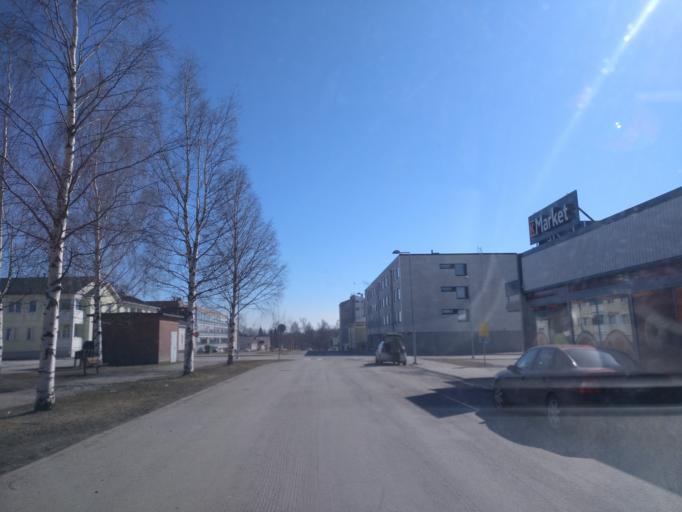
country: FI
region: Lapland
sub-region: Kemi-Tornio
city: Kemi
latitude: 65.7342
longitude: 24.5687
